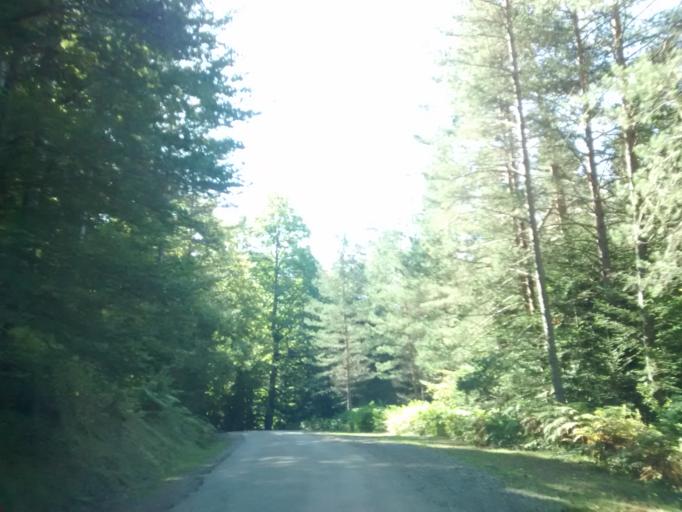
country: ES
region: Aragon
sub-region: Provincia de Huesca
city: Aragues del Puerto
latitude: 42.8401
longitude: -0.7106
